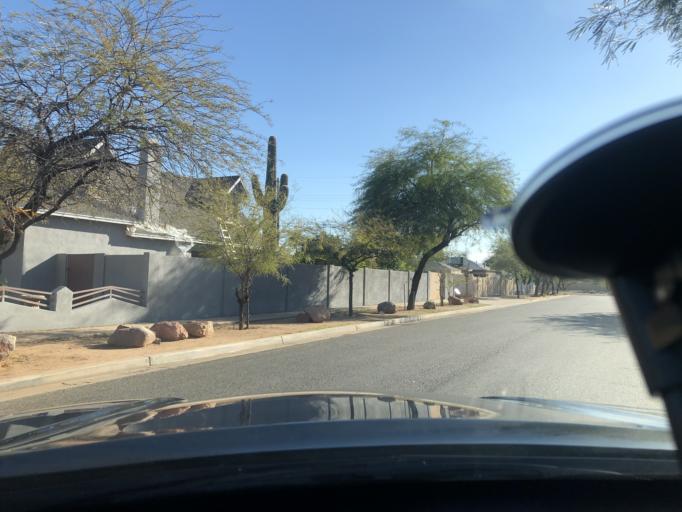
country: US
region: Arizona
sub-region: Maricopa County
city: Phoenix
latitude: 33.4638
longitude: -112.0456
